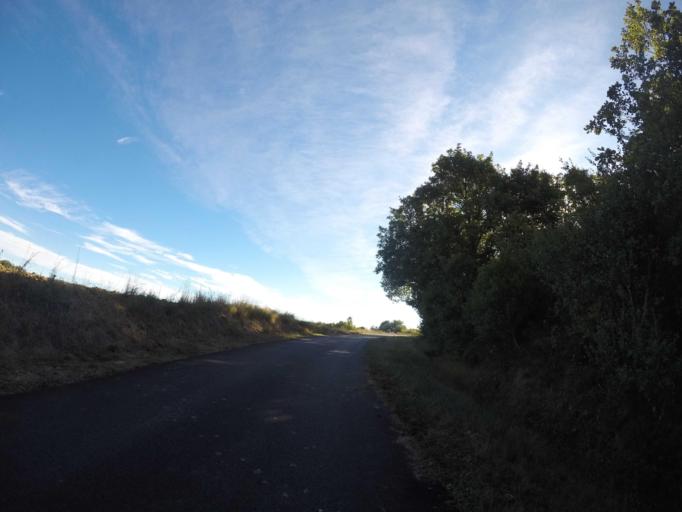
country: FR
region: Languedoc-Roussillon
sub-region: Departement des Pyrenees-Orientales
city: Trouillas
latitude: 42.5789
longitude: 2.7832
